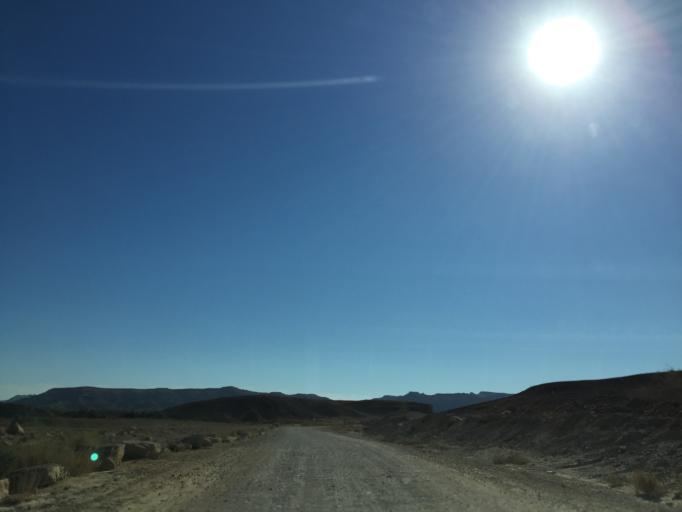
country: IL
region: Southern District
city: Mitzpe Ramon
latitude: 30.6232
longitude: 34.9211
